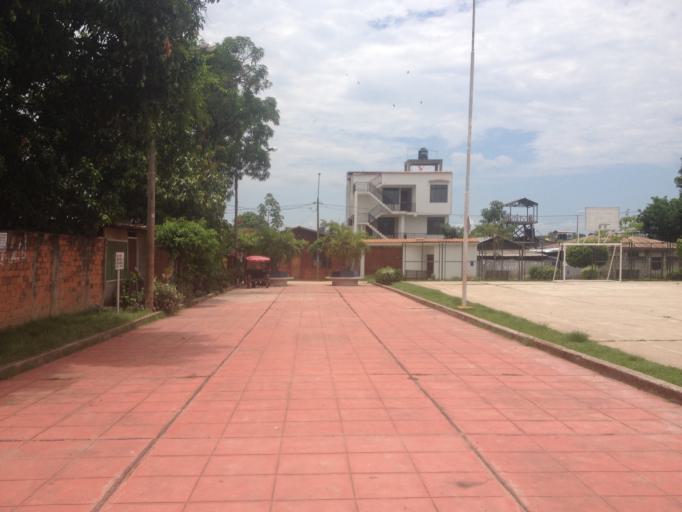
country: PE
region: Ucayali
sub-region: Provincia de Coronel Portillo
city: Pucallpa
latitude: -8.3821
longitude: -74.5586
